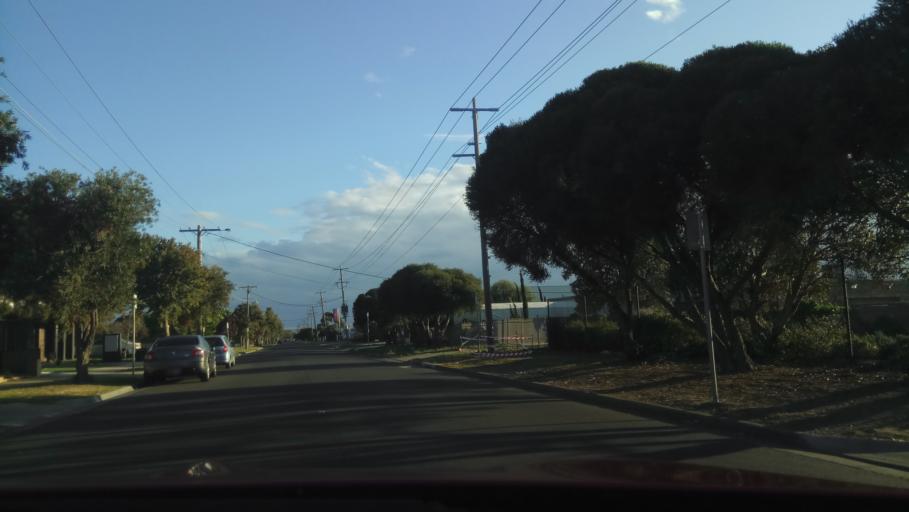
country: AU
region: Victoria
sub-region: Hobsons Bay
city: Altona North
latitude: -37.8385
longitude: 144.8420
